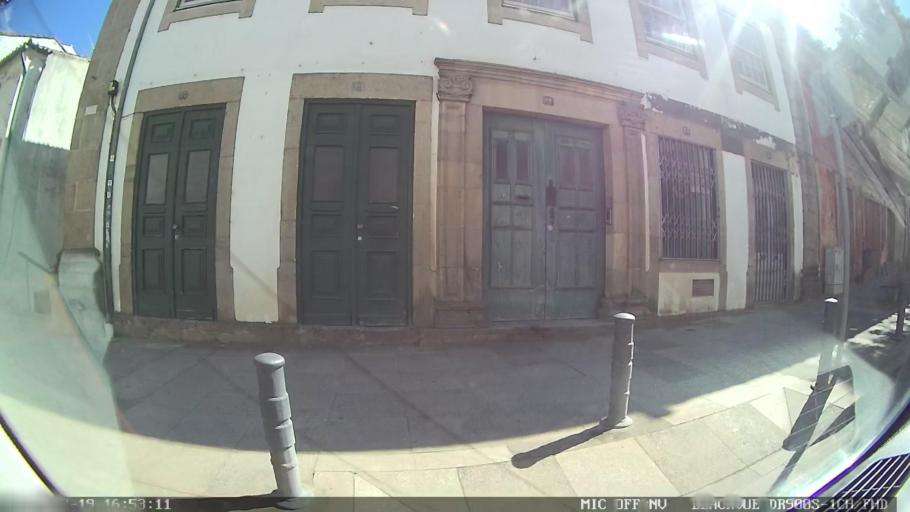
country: PT
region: Braganca
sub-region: Braganca Municipality
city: Braganca
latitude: 41.8055
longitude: -6.7542
